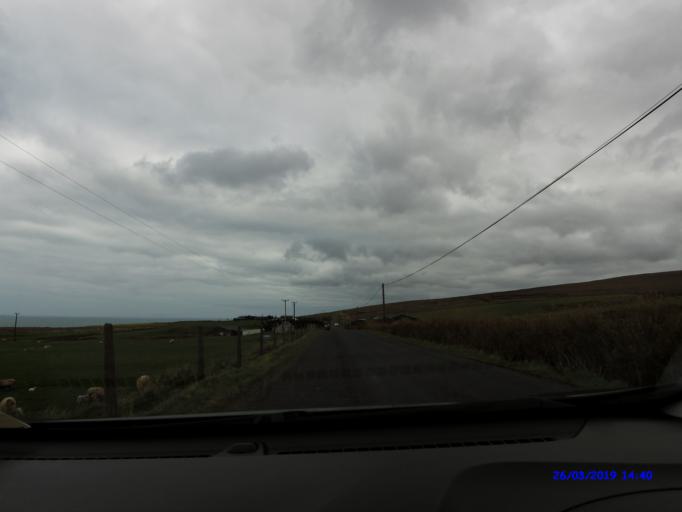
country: IE
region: Connaught
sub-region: Maigh Eo
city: Crossmolina
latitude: 54.3079
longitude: -9.4783
